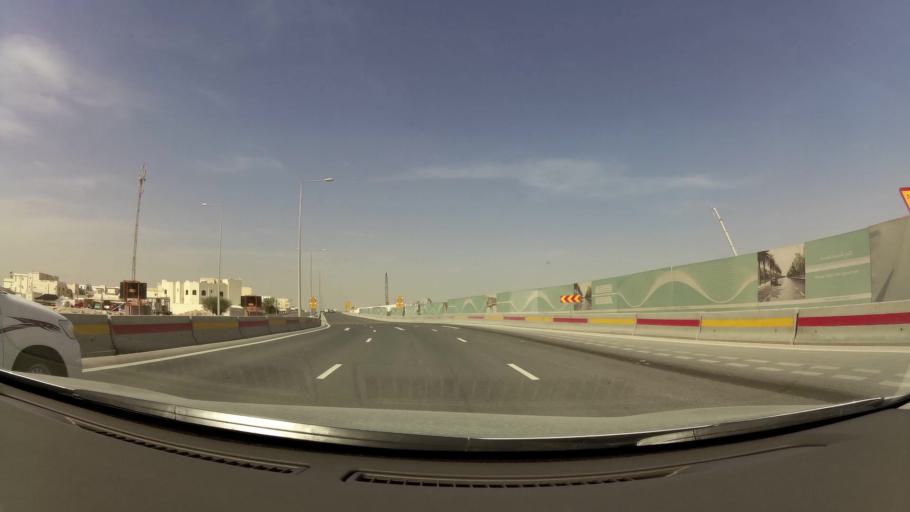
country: QA
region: Baladiyat ar Rayyan
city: Ar Rayyan
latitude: 25.3123
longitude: 51.4155
